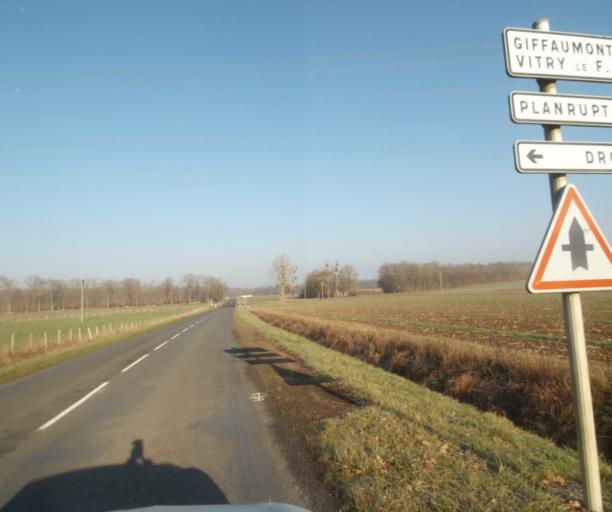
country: FR
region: Champagne-Ardenne
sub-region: Departement de la Haute-Marne
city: Montier-en-Der
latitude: 48.5065
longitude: 4.7484
